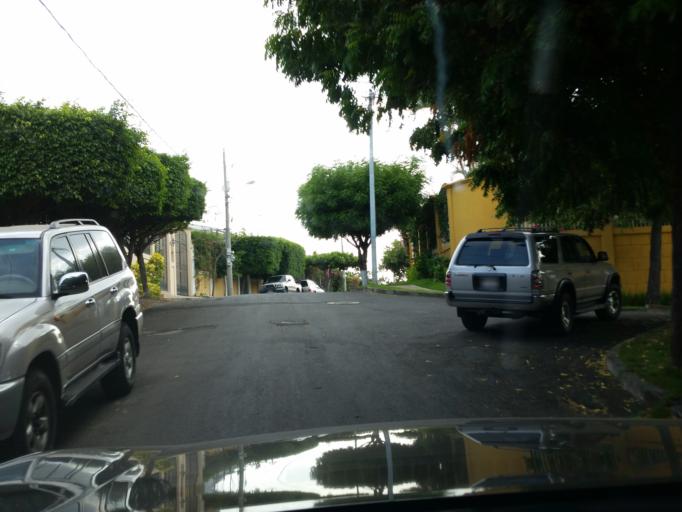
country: NI
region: Managua
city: Managua
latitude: 12.0947
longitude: -86.2445
